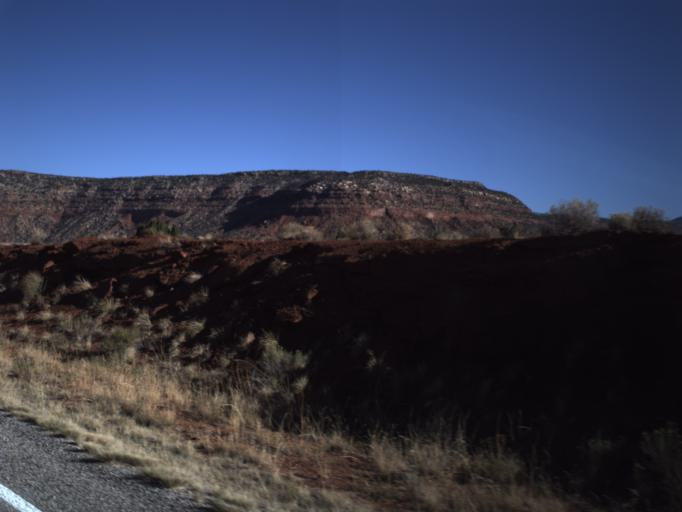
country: US
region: Utah
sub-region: San Juan County
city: Blanding
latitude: 37.5925
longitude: -110.0425
